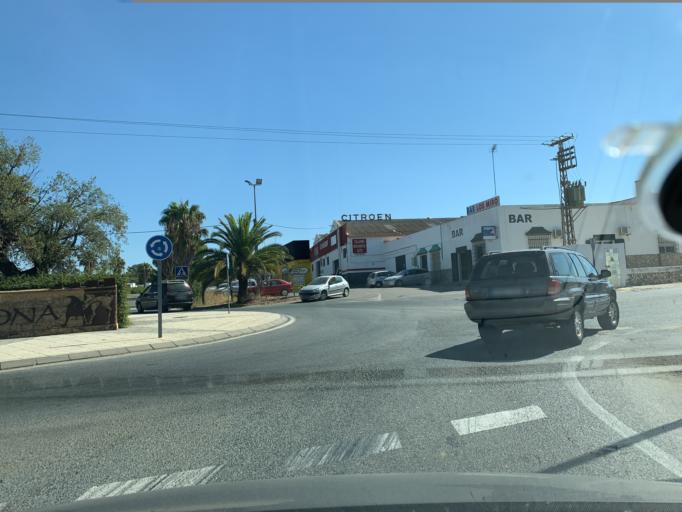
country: ES
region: Andalusia
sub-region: Provincia de Sevilla
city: Carmona
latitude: 37.4686
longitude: -5.6618
